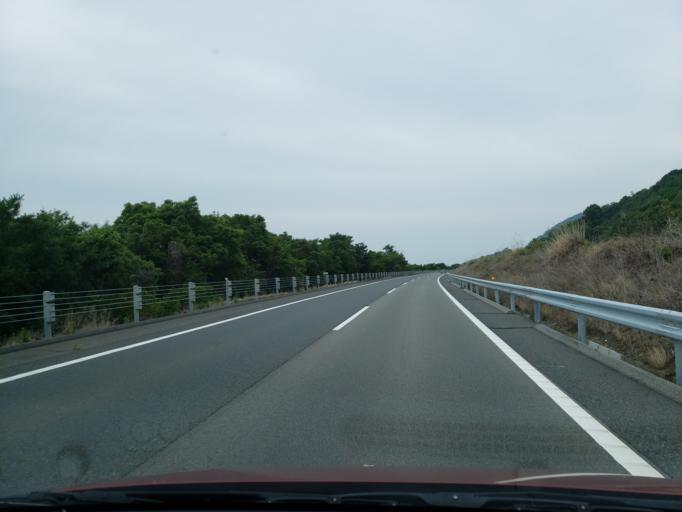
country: JP
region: Hyogo
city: Sumoto
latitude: 34.4880
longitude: 134.8720
